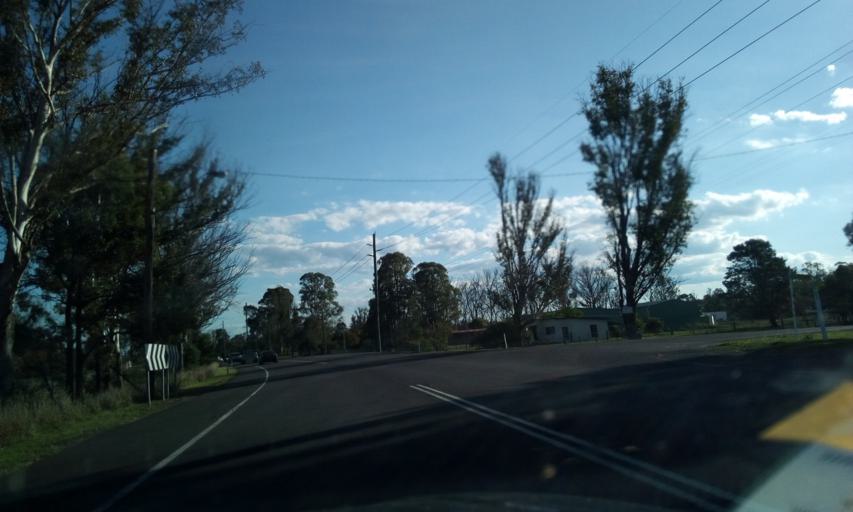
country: AU
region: New South Wales
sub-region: Penrith Municipality
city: Glenmore Park
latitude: -33.8208
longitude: 150.6855
